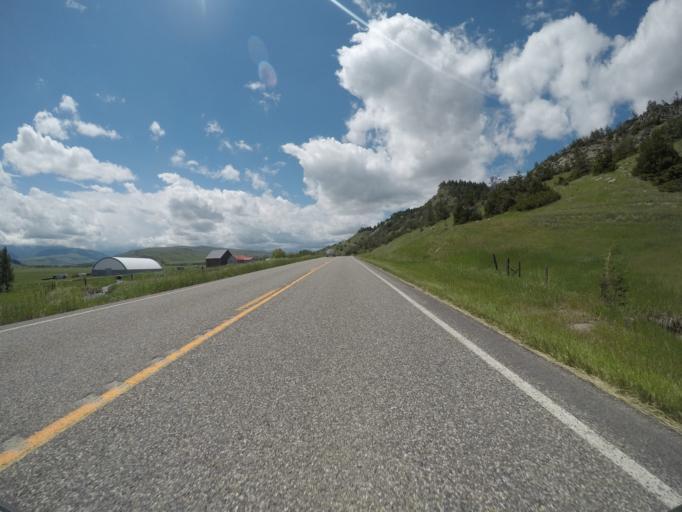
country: US
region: Montana
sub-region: Sweet Grass County
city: Big Timber
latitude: 45.6704
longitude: -110.1002
